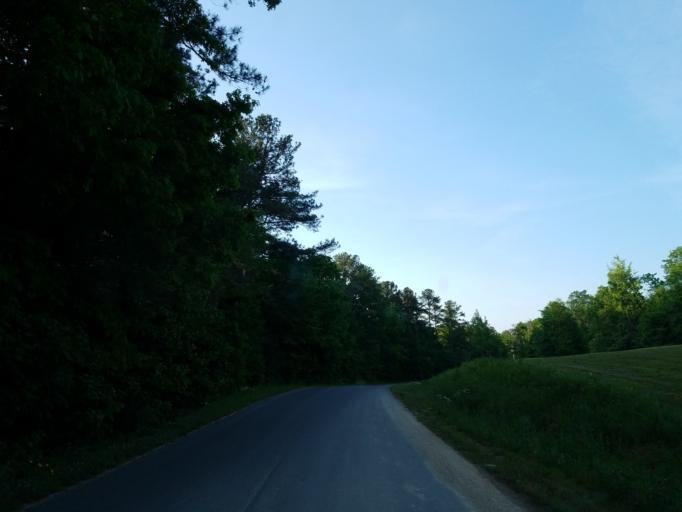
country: US
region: Georgia
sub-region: Whitfield County
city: Dalton
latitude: 34.6639
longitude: -85.0797
